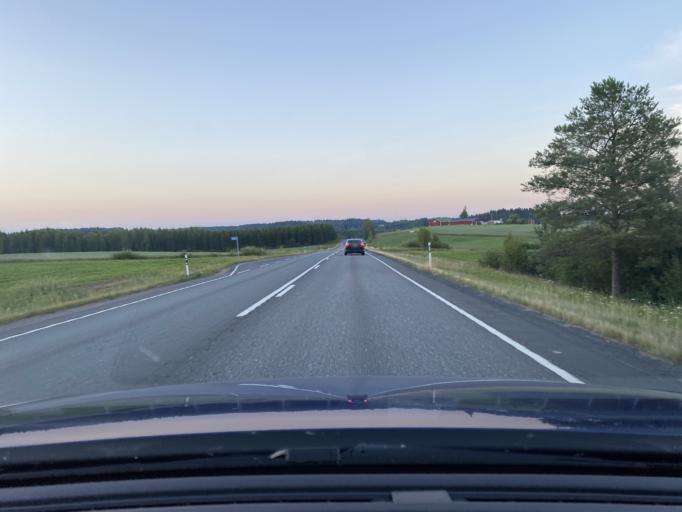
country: FI
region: Pirkanmaa
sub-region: Luoteis-Pirkanmaa
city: Ikaalinen
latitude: 61.8596
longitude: 22.9506
